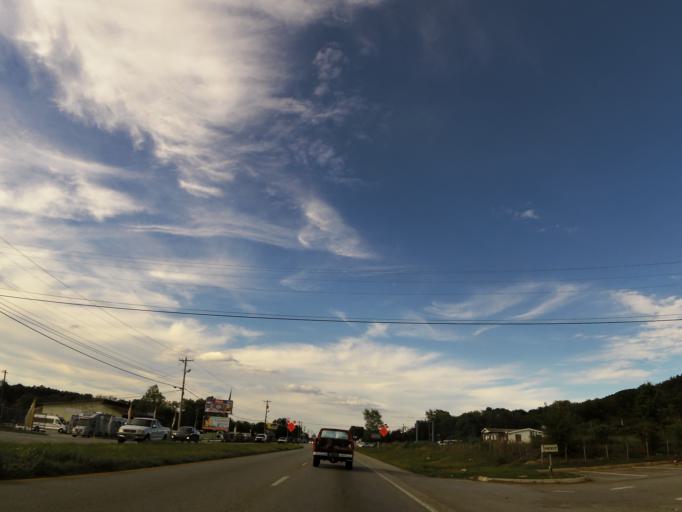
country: US
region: Tennessee
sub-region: Blount County
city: Alcoa
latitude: 35.8498
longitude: -83.9635
